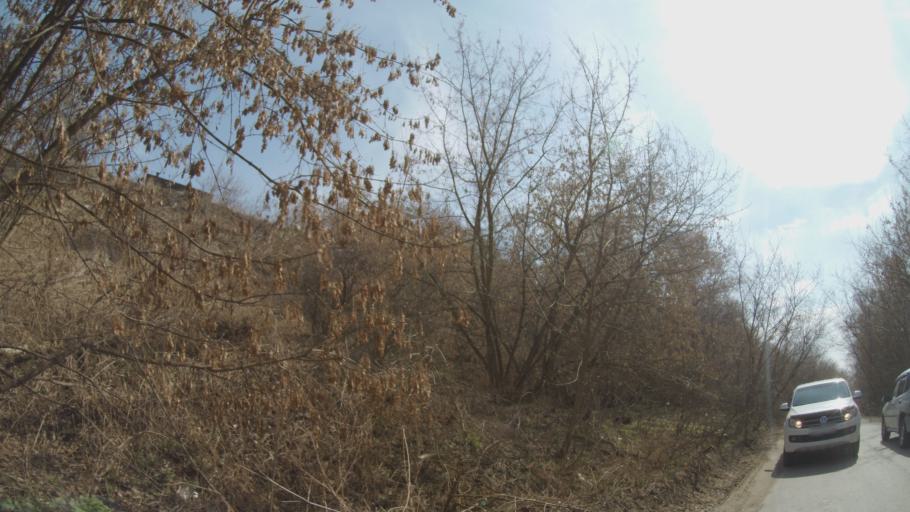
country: RU
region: Nizjnij Novgorod
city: Vyyezdnoye
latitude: 55.3883
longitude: 43.8099
